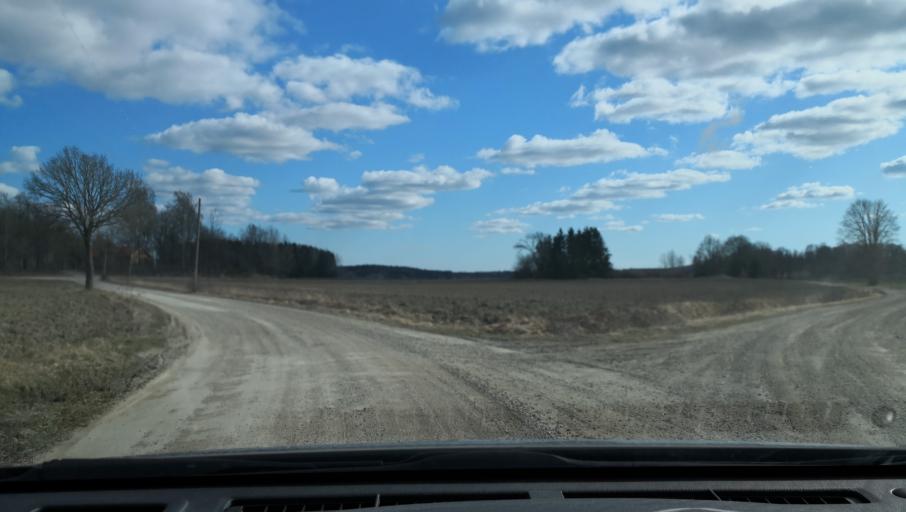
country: SE
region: Soedermanland
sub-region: Katrineholms Kommun
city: Katrineholm
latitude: 59.1429
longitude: 16.0778
